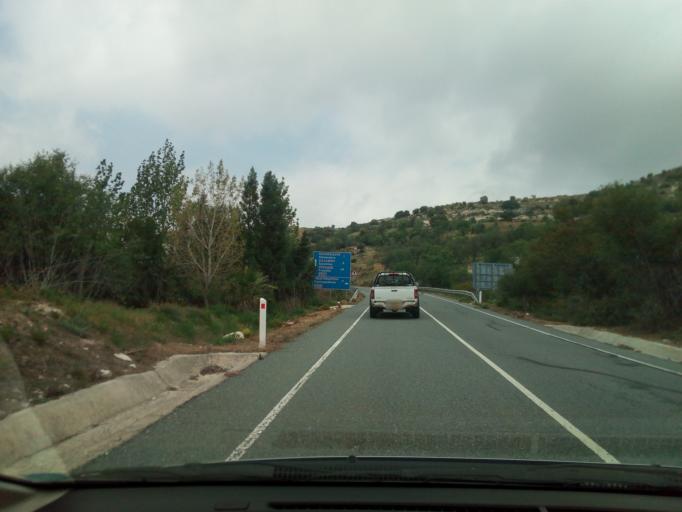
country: CY
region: Limassol
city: Pissouri
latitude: 34.8009
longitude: 32.6493
